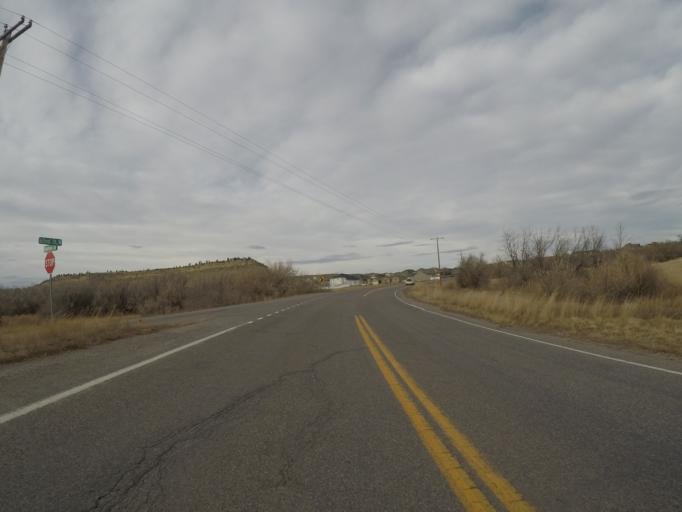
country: US
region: Montana
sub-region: Yellowstone County
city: Laurel
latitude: 45.8002
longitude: -108.6733
